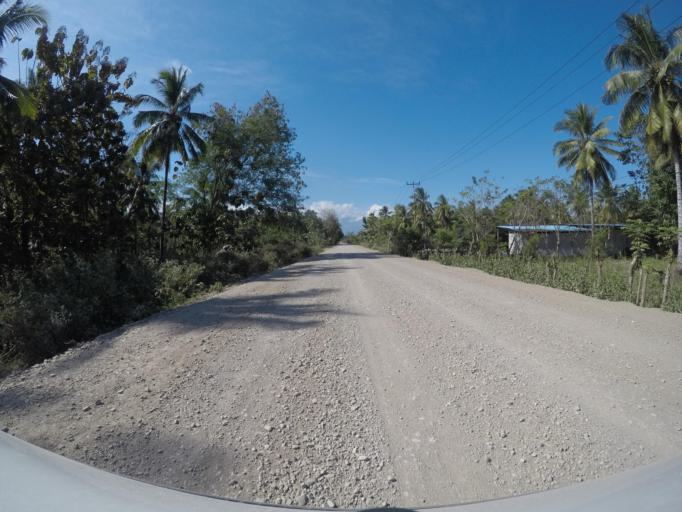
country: TL
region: Viqueque
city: Viqueque
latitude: -8.8576
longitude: 126.5103
